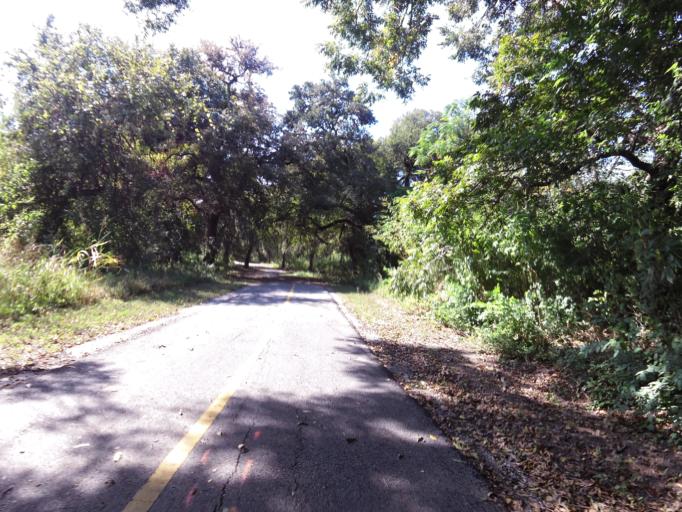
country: US
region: Texas
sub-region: Bexar County
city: San Antonio
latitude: 29.4038
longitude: -98.4280
